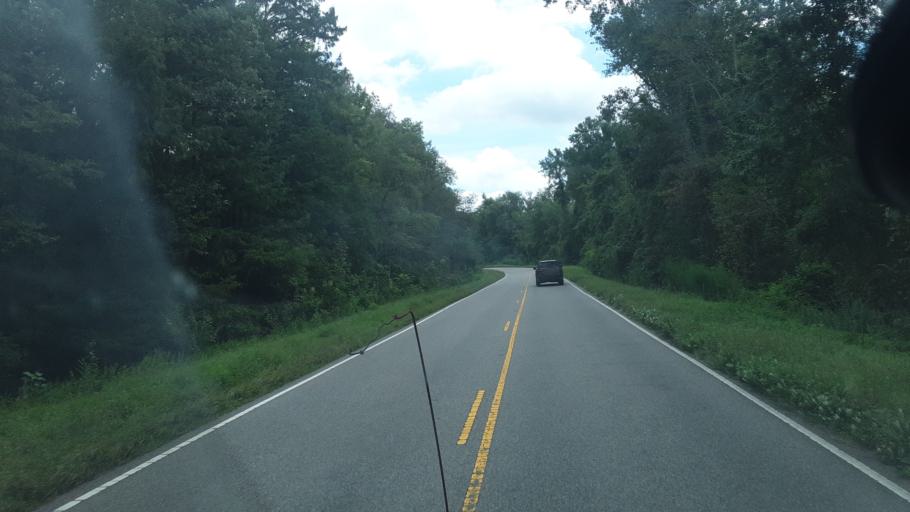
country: US
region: North Carolina
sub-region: Robeson County
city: Fairmont
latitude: 34.3477
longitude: -79.0775
